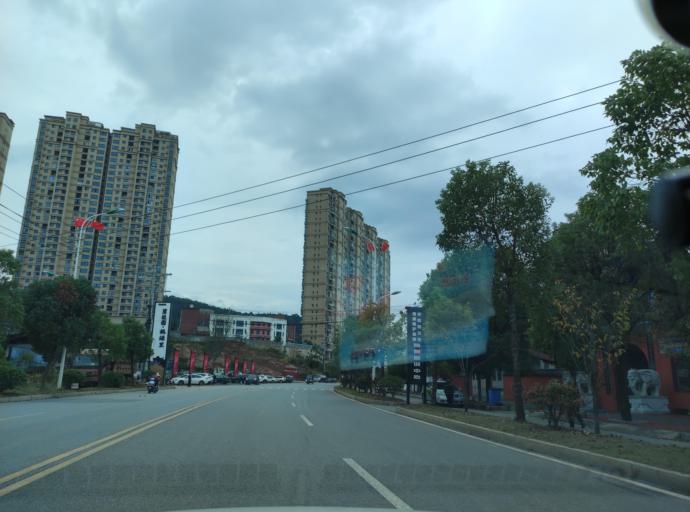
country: CN
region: Jiangxi Sheng
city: Pingxiang
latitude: 27.6812
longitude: 113.9093
